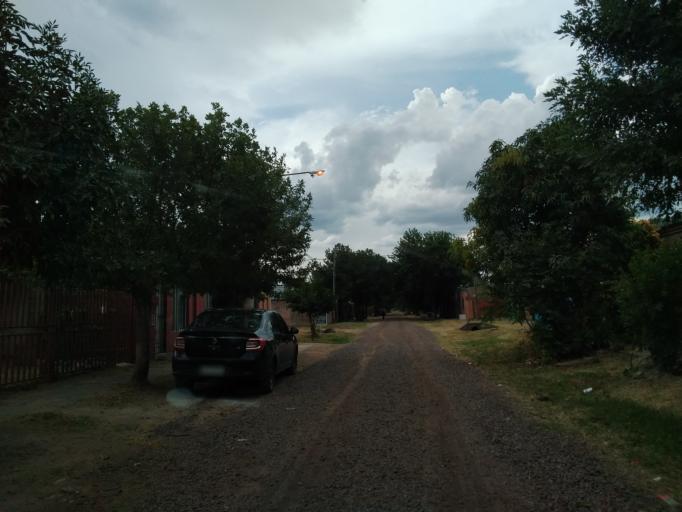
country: AR
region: Corrientes
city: Corrientes
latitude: -27.5208
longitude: -58.7901
